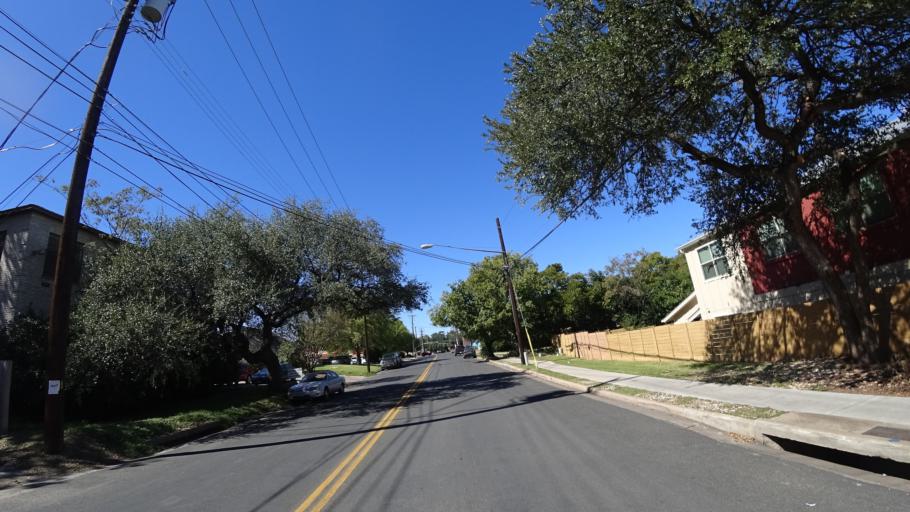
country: US
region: Texas
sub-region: Travis County
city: Rollingwood
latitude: 30.2302
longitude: -97.7858
